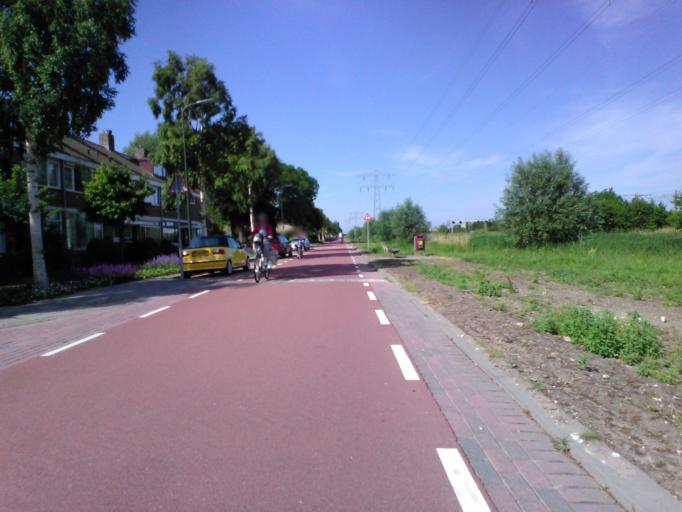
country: NL
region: South Holland
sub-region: Gemeente Leidschendam-Voorburg
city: Voorburg
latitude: 52.0978
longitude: 4.3872
